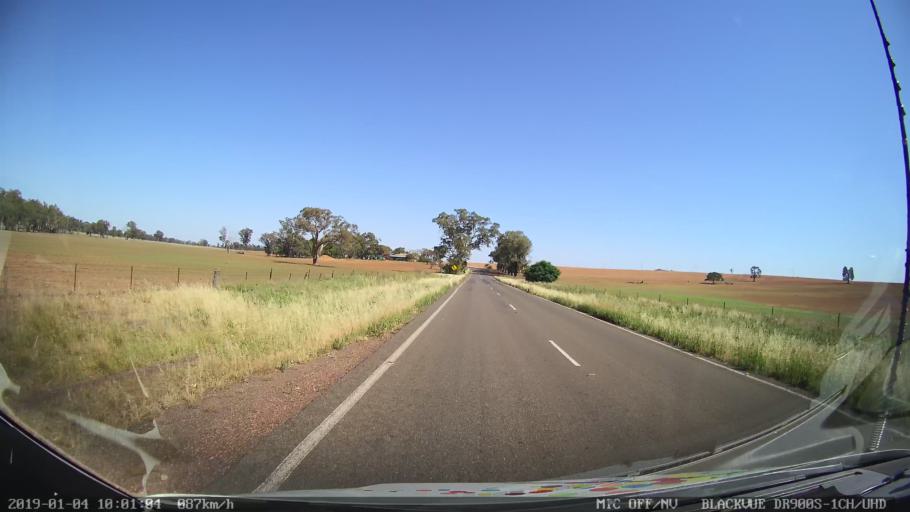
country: AU
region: New South Wales
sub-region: Cabonne
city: Canowindra
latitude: -33.4906
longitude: 148.3744
